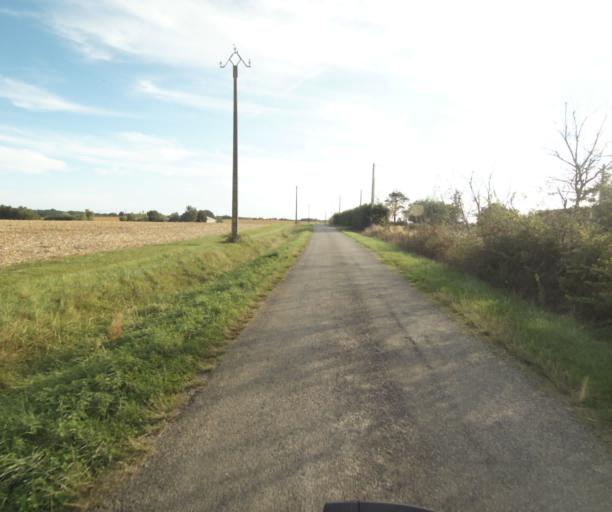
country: FR
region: Midi-Pyrenees
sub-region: Departement du Tarn-et-Garonne
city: Finhan
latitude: 43.9138
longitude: 1.1312
